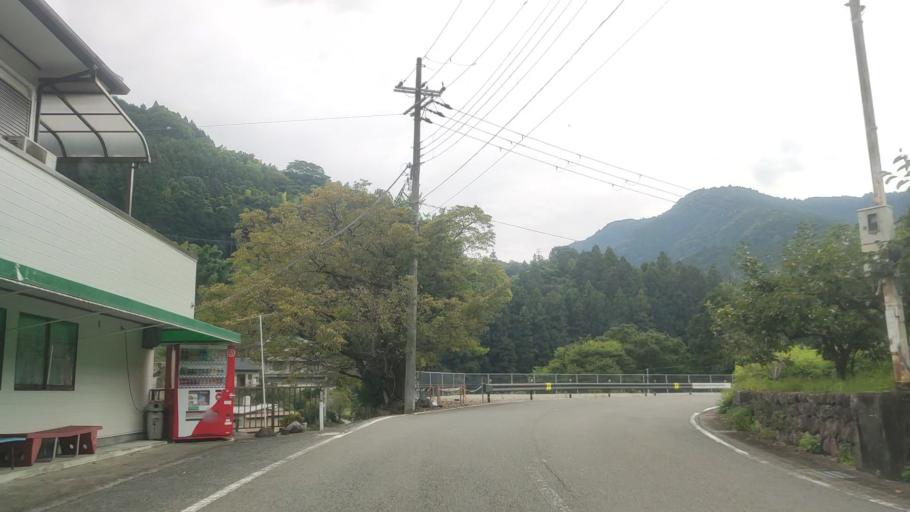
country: JP
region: Wakayama
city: Koya
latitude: 34.2589
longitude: 135.5469
